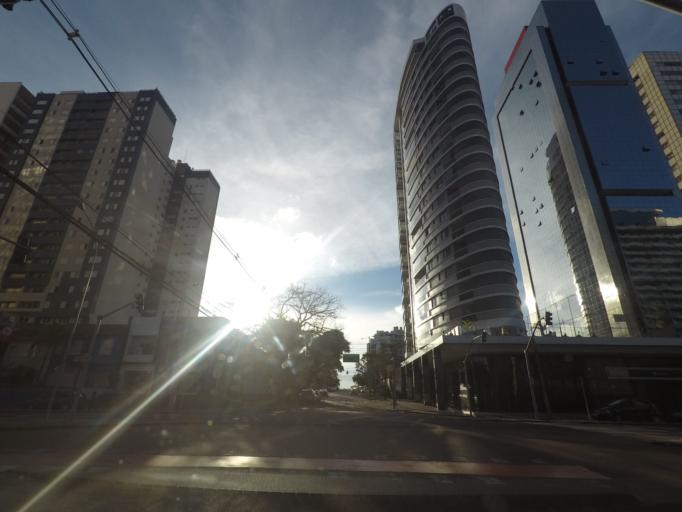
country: BR
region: Parana
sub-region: Curitiba
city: Curitiba
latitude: -25.4168
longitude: -49.2619
